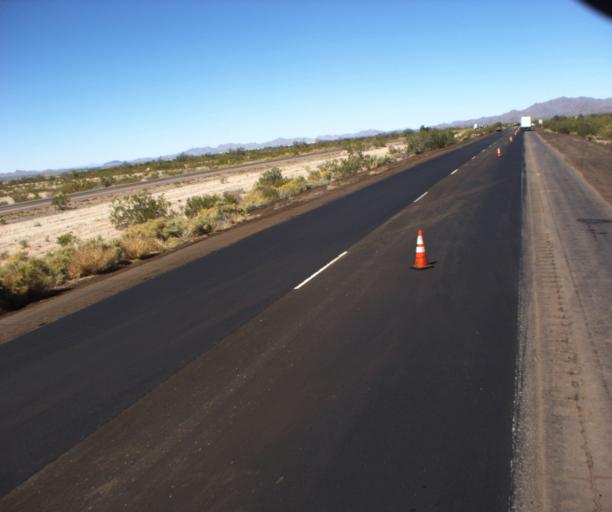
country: US
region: Arizona
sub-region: Maricopa County
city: Gila Bend
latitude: 33.0300
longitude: -112.6475
